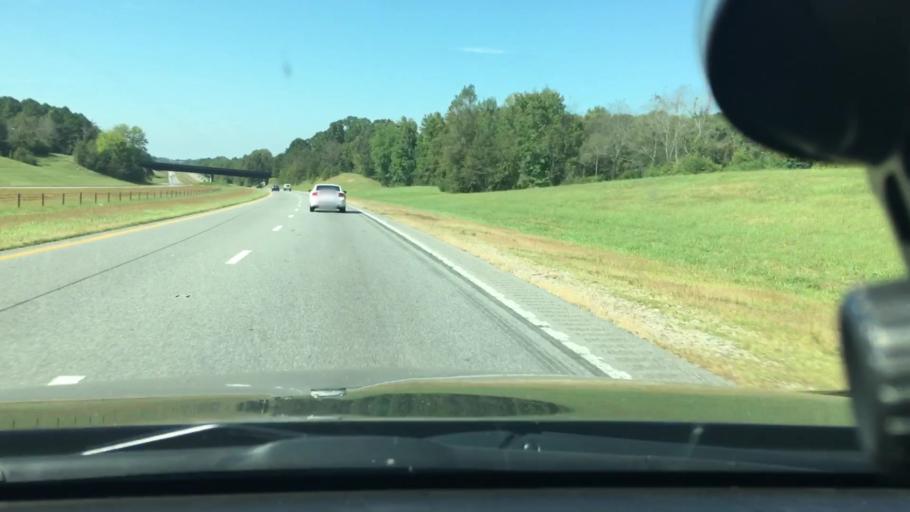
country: US
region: North Carolina
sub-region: Cleveland County
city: White Plains
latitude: 35.2595
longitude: -81.3739
